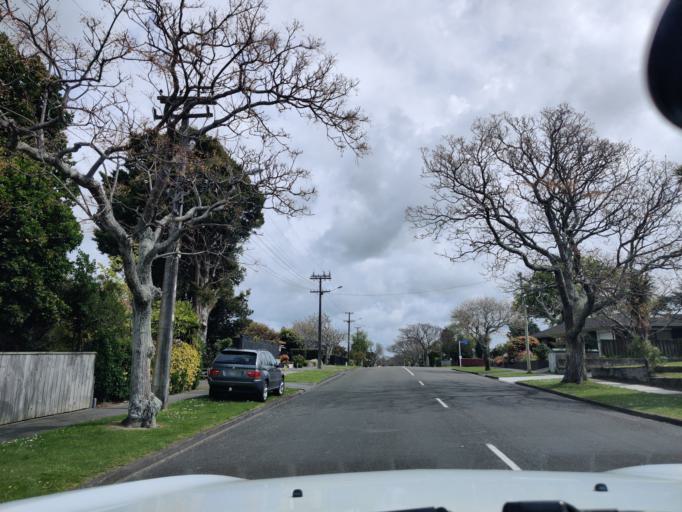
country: NZ
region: Manawatu-Wanganui
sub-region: Palmerston North City
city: Palmerston North
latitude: -40.3793
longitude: 175.5932
